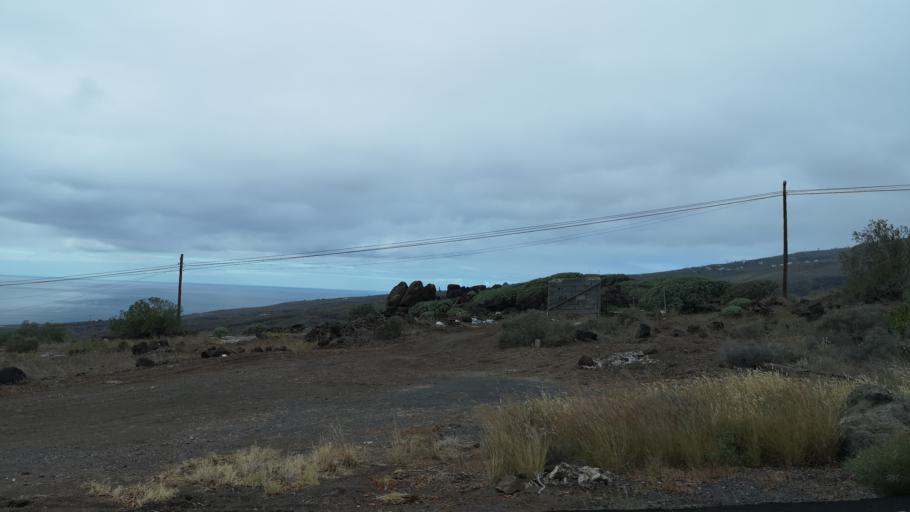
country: ES
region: Canary Islands
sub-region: Provincia de Santa Cruz de Tenerife
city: Alajero
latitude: 28.0501
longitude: -17.1990
